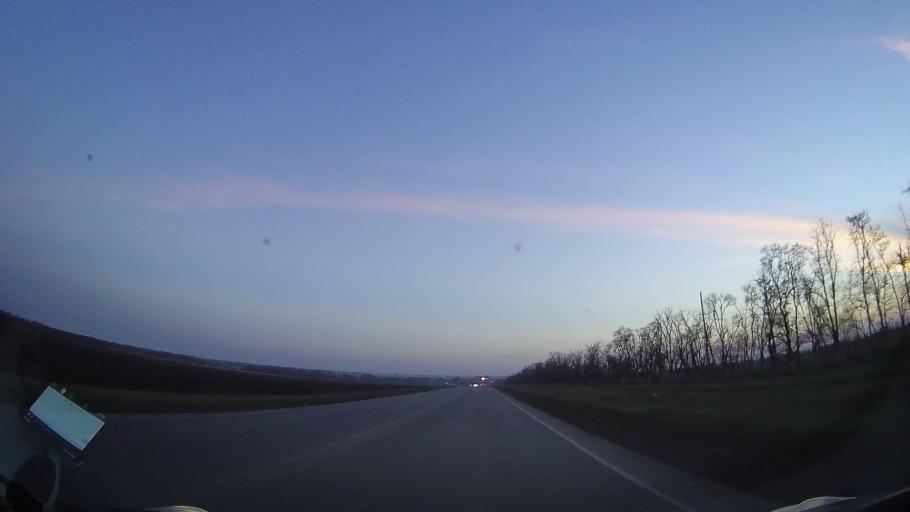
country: RU
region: Rostov
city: Zernograd
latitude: 46.8180
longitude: 40.2994
